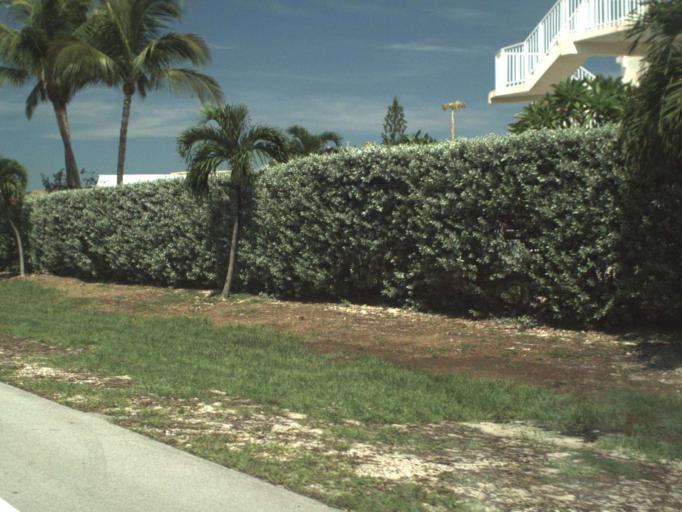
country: US
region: Florida
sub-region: Monroe County
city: Islamorada
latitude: 24.8060
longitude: -80.8424
